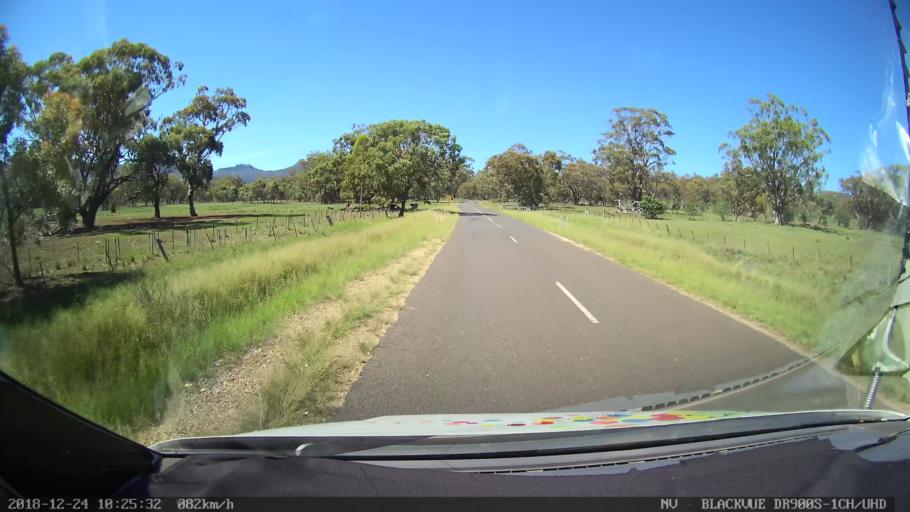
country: AU
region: New South Wales
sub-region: Liverpool Plains
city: Quirindi
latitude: -31.8001
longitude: 150.5281
